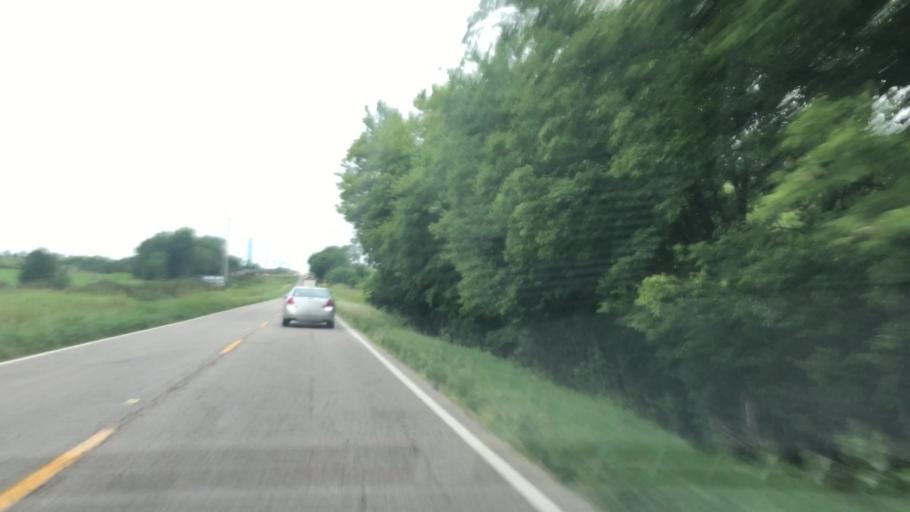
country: US
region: Oklahoma
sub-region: Washington County
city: Dewey
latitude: 36.7280
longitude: -95.8491
